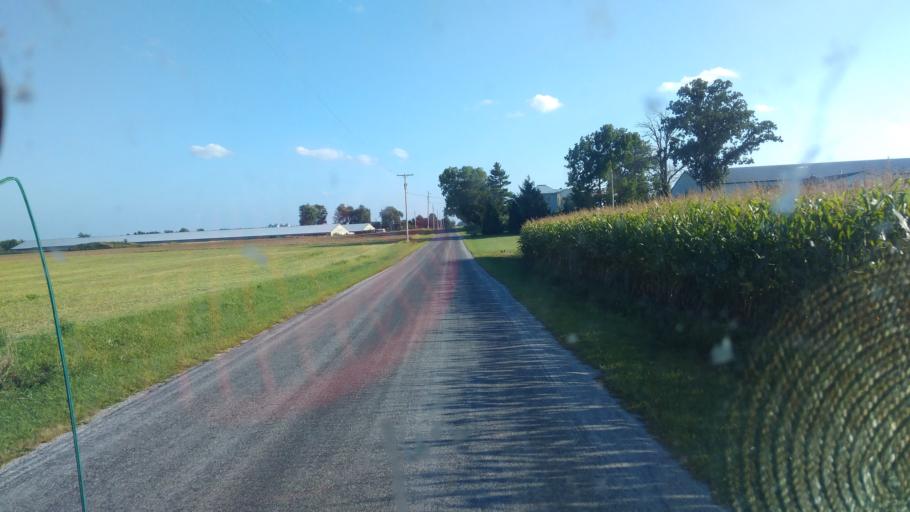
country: US
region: Ohio
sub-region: Huron County
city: Greenwich
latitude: 40.9581
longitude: -82.4512
